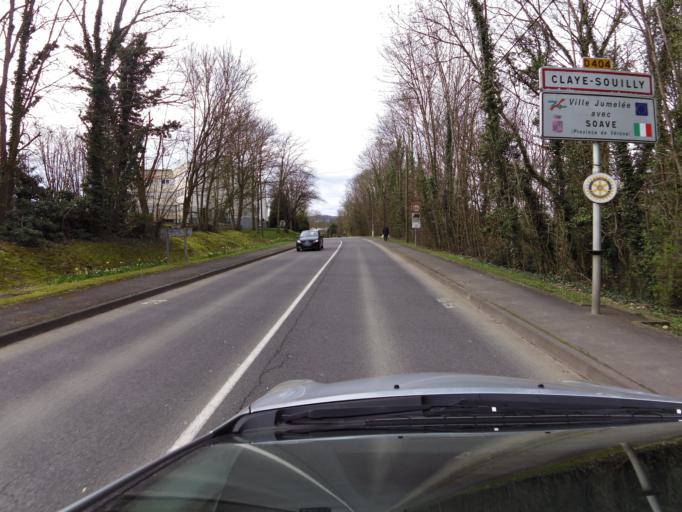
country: FR
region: Ile-de-France
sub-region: Departement de Seine-et-Marne
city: Claye-Souilly
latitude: 48.9483
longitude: 2.6914
